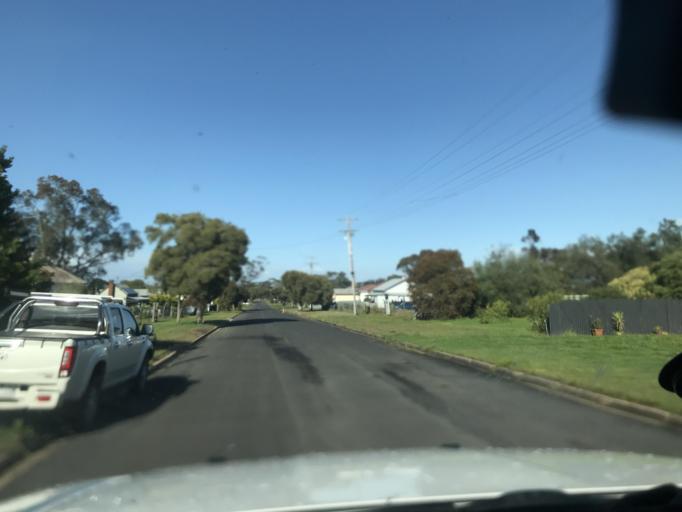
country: AU
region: Victoria
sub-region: Horsham
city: Horsham
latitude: -36.7203
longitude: 141.4758
